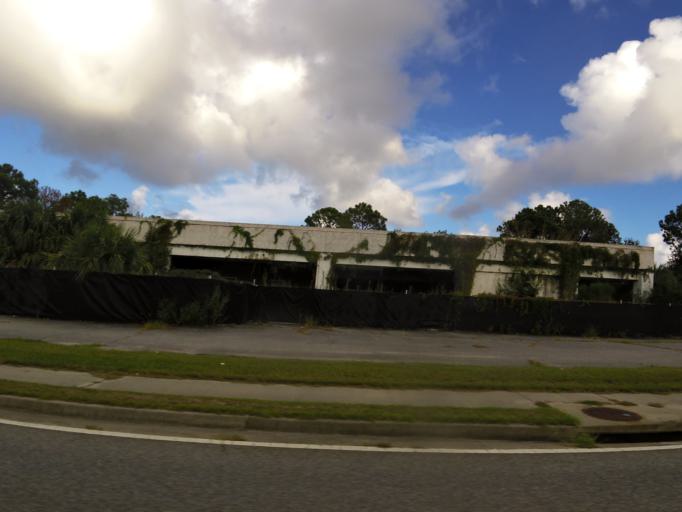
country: US
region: Georgia
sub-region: Glynn County
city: Brunswick
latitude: 31.1787
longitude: -81.4724
